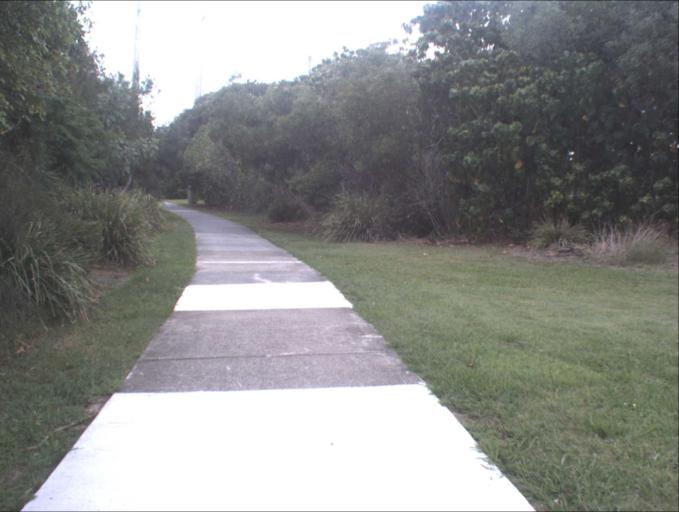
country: AU
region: Queensland
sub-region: Logan
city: Slacks Creek
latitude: -27.6436
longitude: 153.1355
